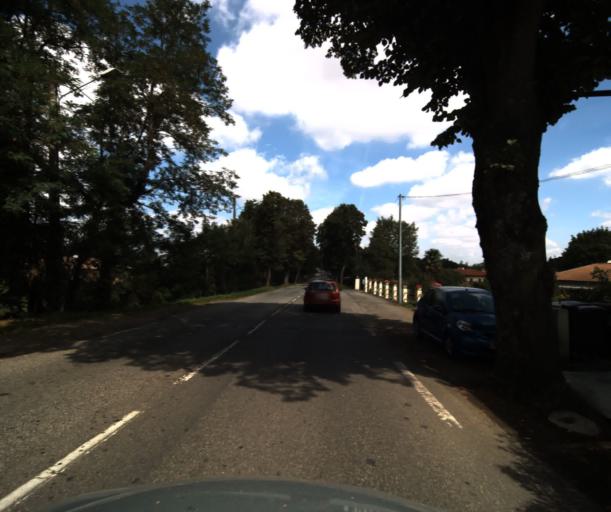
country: FR
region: Midi-Pyrenees
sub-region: Departement de la Haute-Garonne
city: Pinsaguel
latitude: 43.5134
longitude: 1.3878
